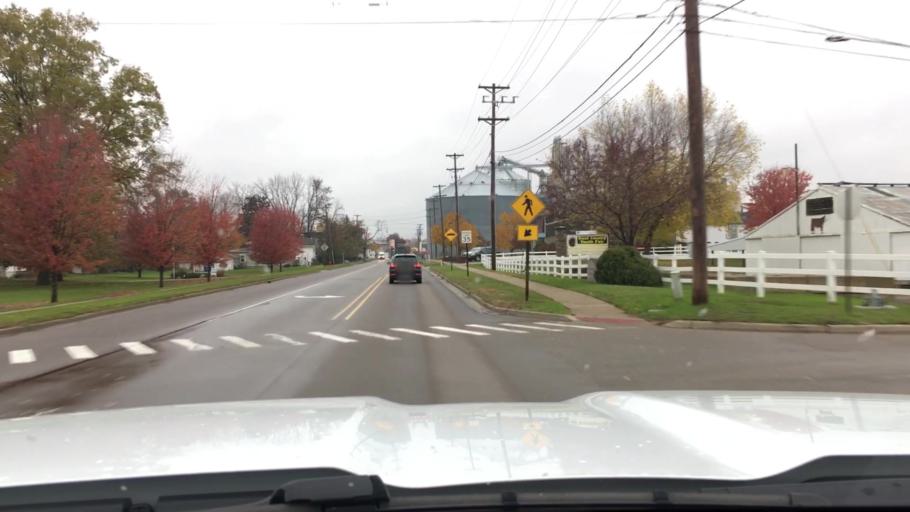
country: US
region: Michigan
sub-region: Kent County
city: Lowell
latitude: 42.9293
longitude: -85.3426
